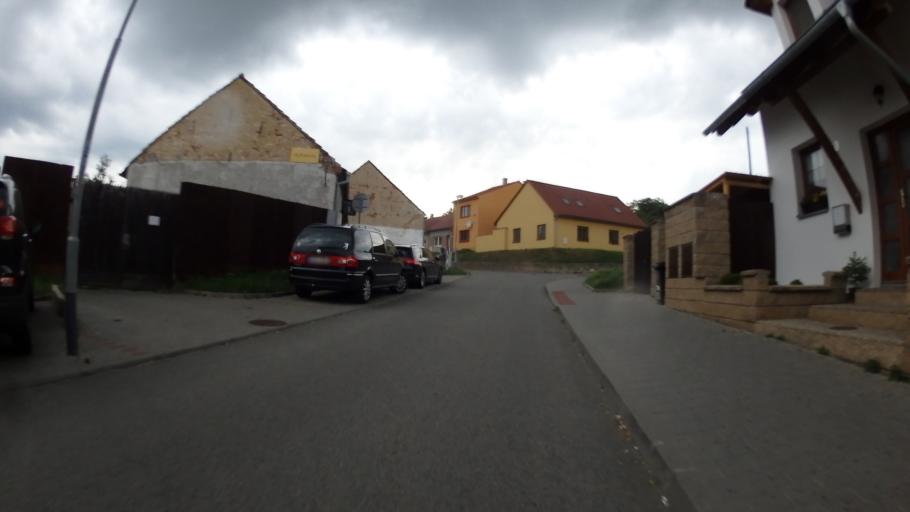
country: CZ
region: South Moravian
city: Ostopovice
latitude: 49.1653
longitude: 16.5642
